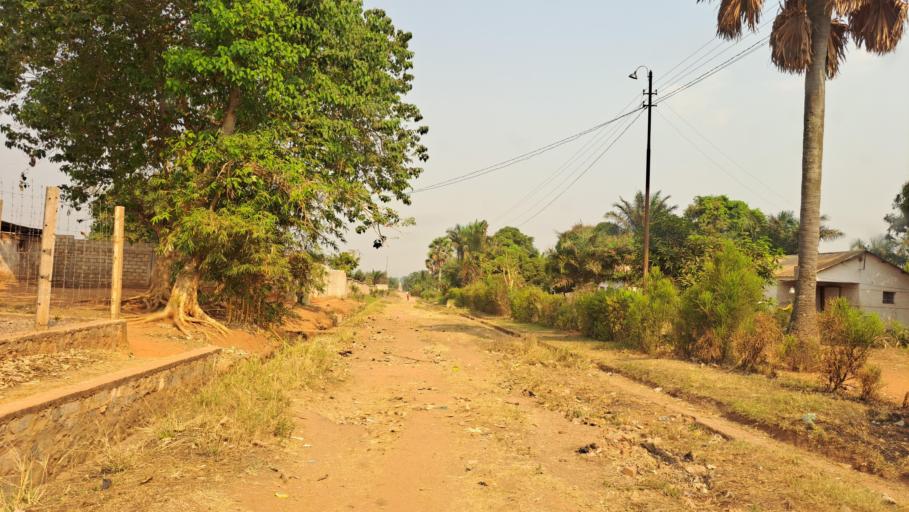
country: CD
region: Kasai-Oriental
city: Mbuji-Mayi
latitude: -6.1321
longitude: 23.5863
